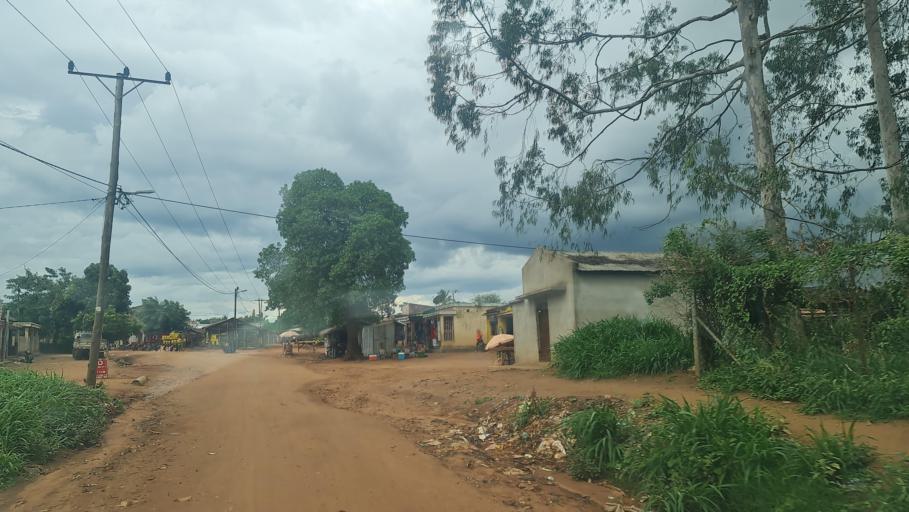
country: MW
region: Southern Region
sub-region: Nsanje District
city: Nsanje
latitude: -17.3346
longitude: 35.5960
